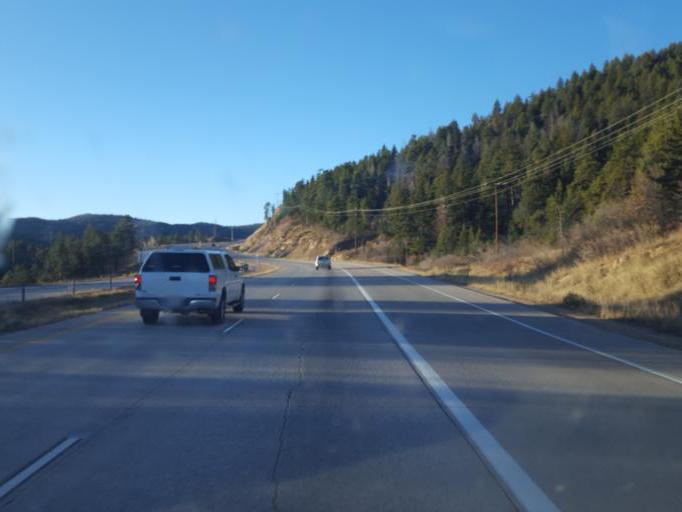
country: US
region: Colorado
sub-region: Jefferson County
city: Indian Hills
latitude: 39.5625
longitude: -105.2395
